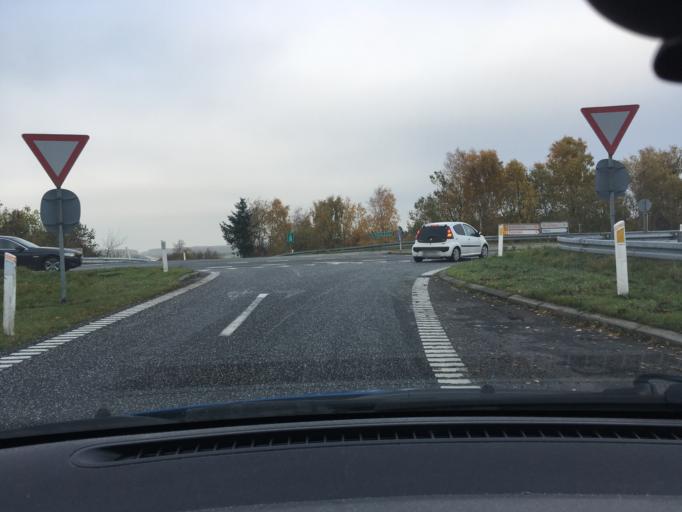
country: DK
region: South Denmark
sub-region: Aabenraa Kommune
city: Aabenraa
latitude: 54.9828
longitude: 9.3807
